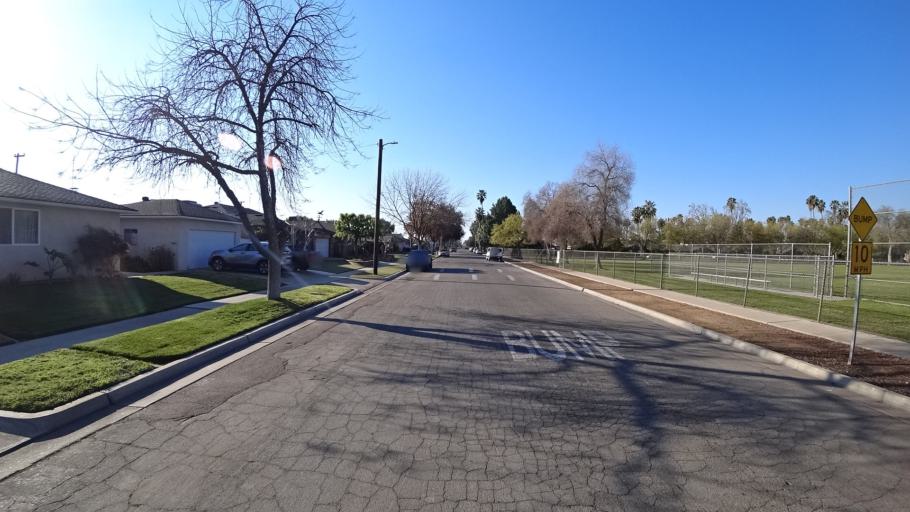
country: US
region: California
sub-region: Fresno County
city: Fresno
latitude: 36.8184
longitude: -119.7768
